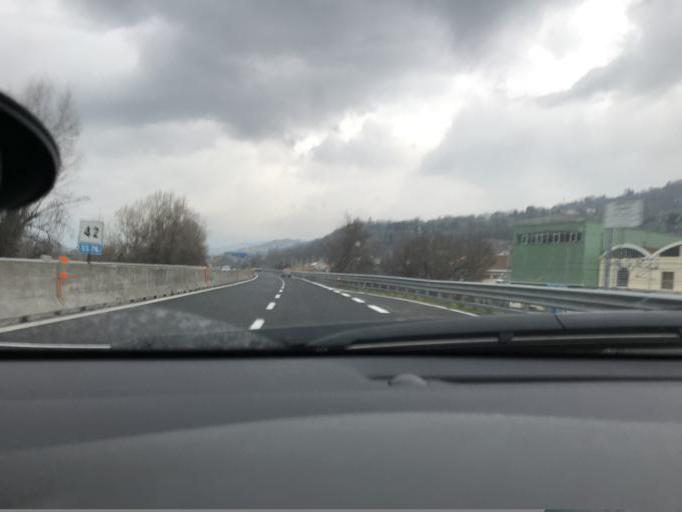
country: IT
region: The Marches
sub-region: Provincia di Ancona
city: Macine-Borgo Loreto
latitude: 43.4804
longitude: 13.0834
